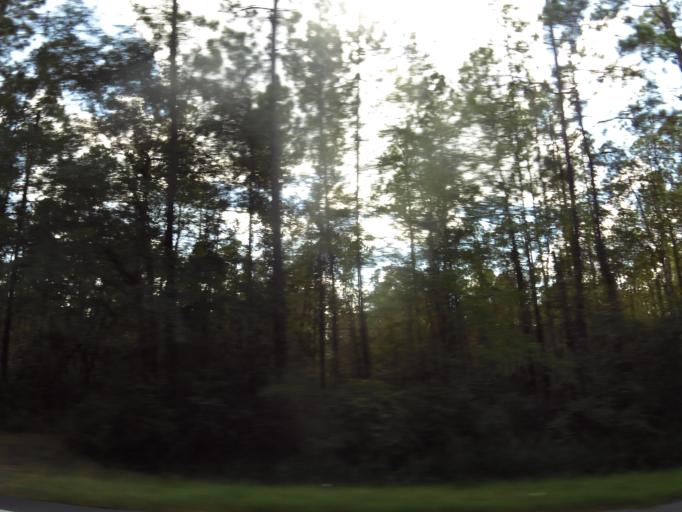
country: US
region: Georgia
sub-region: Echols County
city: Statenville
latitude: 30.7514
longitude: -83.1111
